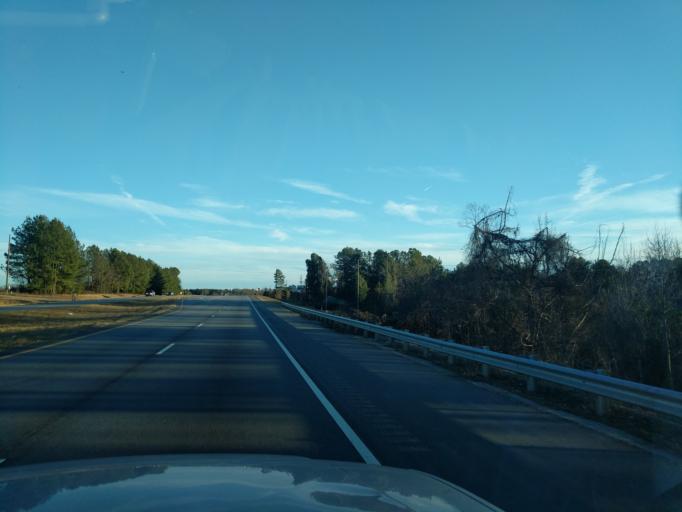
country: US
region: Georgia
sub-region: Franklin County
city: Lavonia
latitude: 34.4663
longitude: -83.1722
